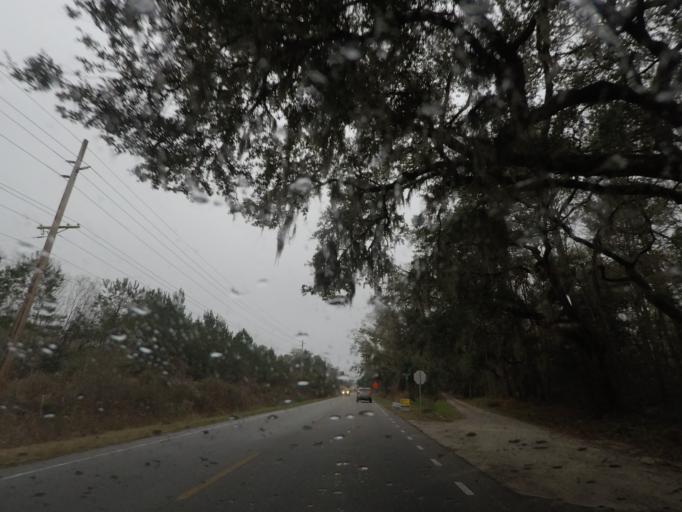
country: US
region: South Carolina
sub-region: Charleston County
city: Seabrook Island
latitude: 32.5658
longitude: -80.2818
